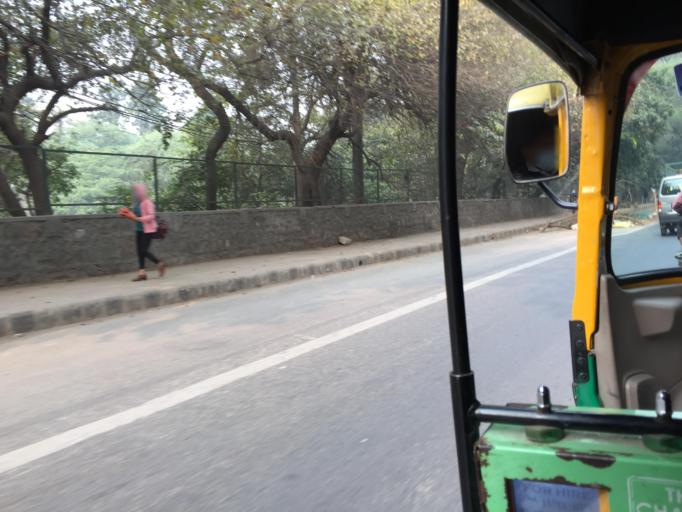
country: IN
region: NCT
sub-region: New Delhi
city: New Delhi
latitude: 28.5142
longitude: 77.1862
